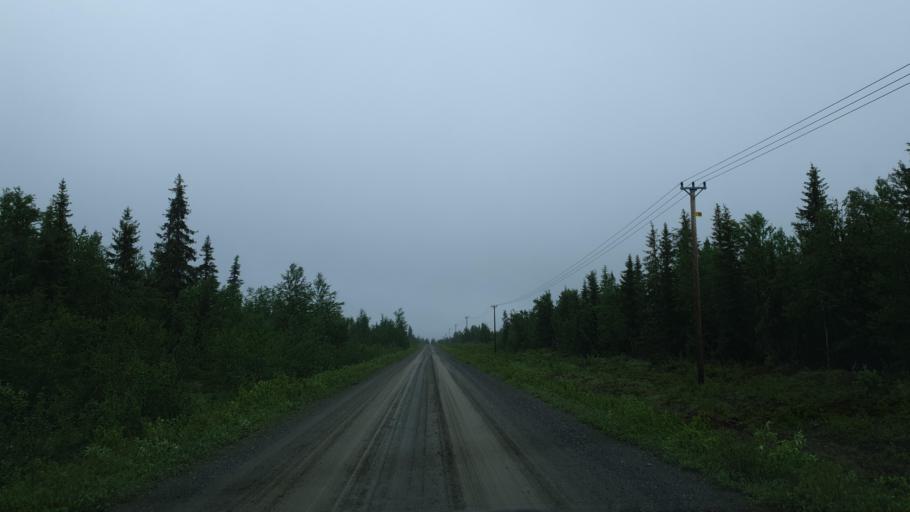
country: SE
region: Vaesterbotten
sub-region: Vilhelmina Kommun
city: Sjoberg
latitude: 65.3146
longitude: 15.9593
